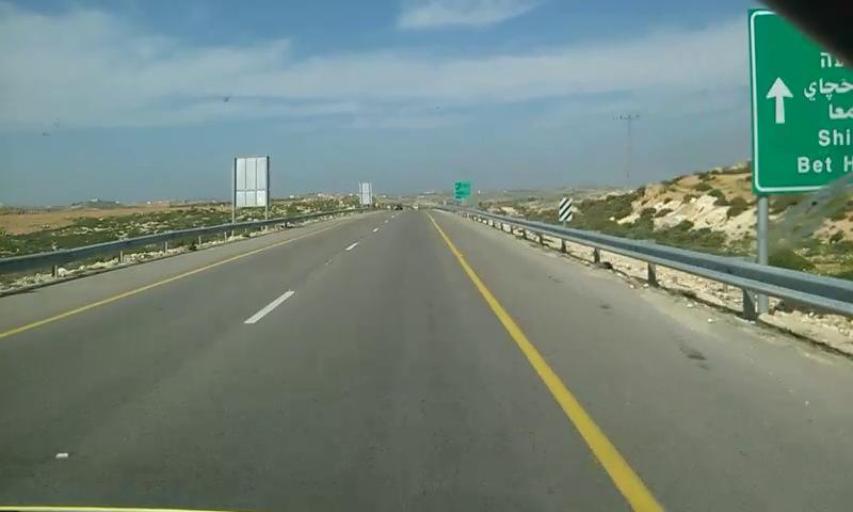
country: PS
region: West Bank
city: Az Zahiriyah
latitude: 31.3811
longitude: 35.0048
